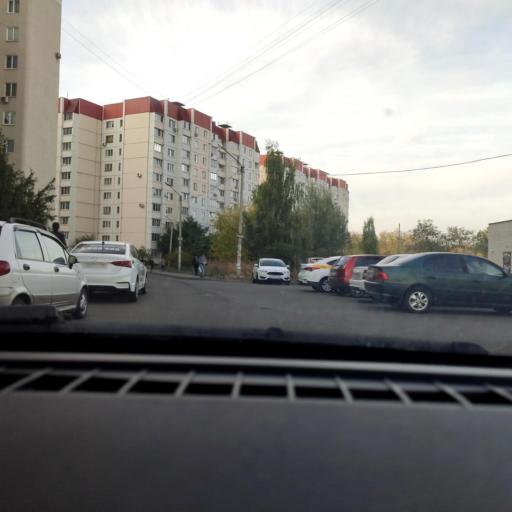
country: RU
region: Voronezj
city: Podgornoye
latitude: 51.7296
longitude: 39.2044
